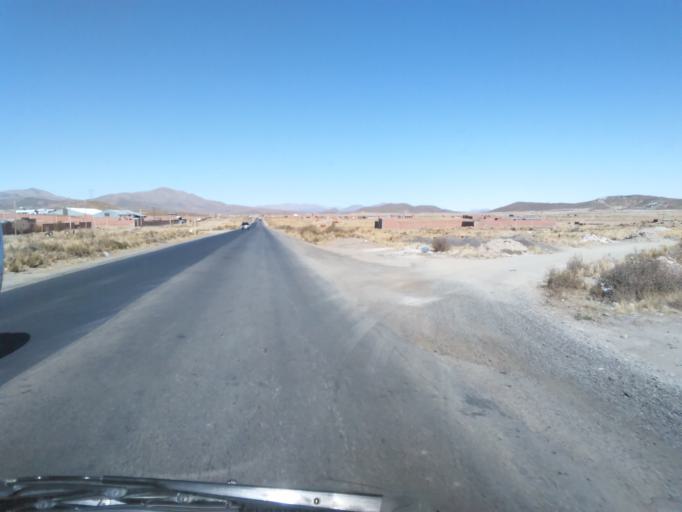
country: BO
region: Oruro
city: Oruro
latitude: -17.9987
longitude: -67.0440
